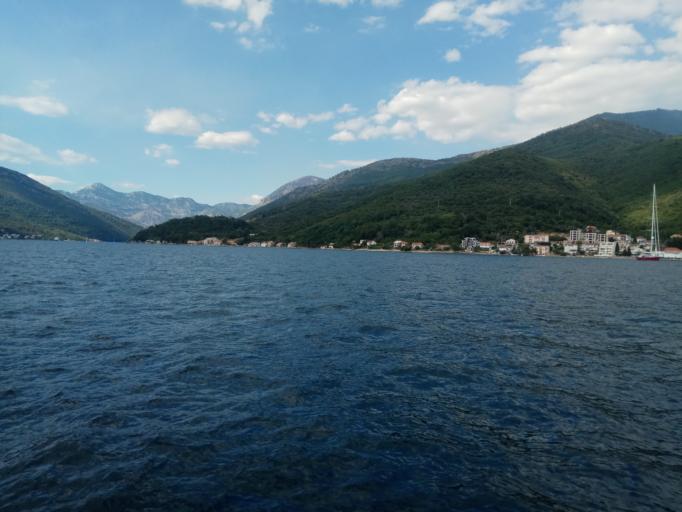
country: ME
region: Tivat
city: Tivat
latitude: 42.4446
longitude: 18.6806
